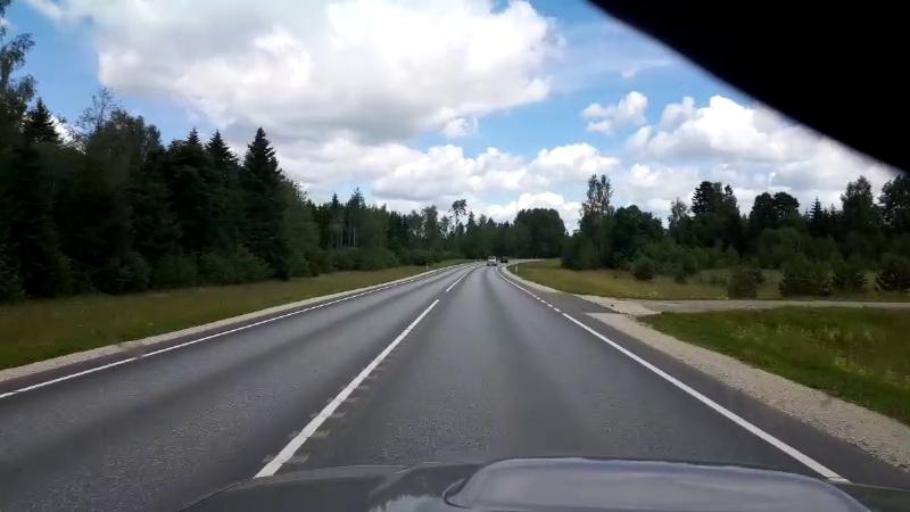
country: EE
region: Laeaene-Virumaa
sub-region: Tapa vald
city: Tapa
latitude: 59.2797
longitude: 26.0408
